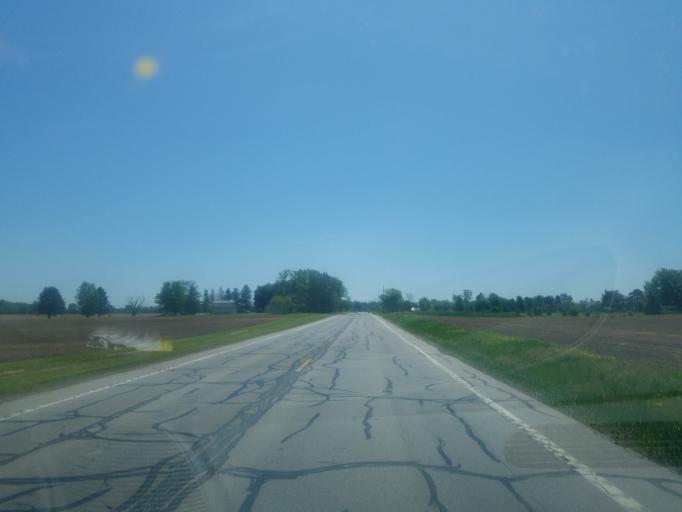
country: US
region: Ohio
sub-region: Huron County
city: New London
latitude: 41.0730
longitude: -82.4596
